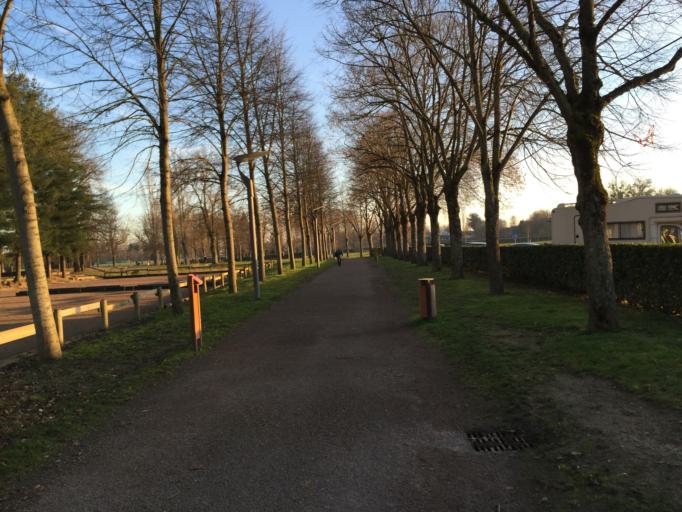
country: FR
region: Bourgogne
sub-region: Departement de Saone-et-Loire
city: Paray-le-Monial
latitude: 46.4480
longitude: 4.1206
